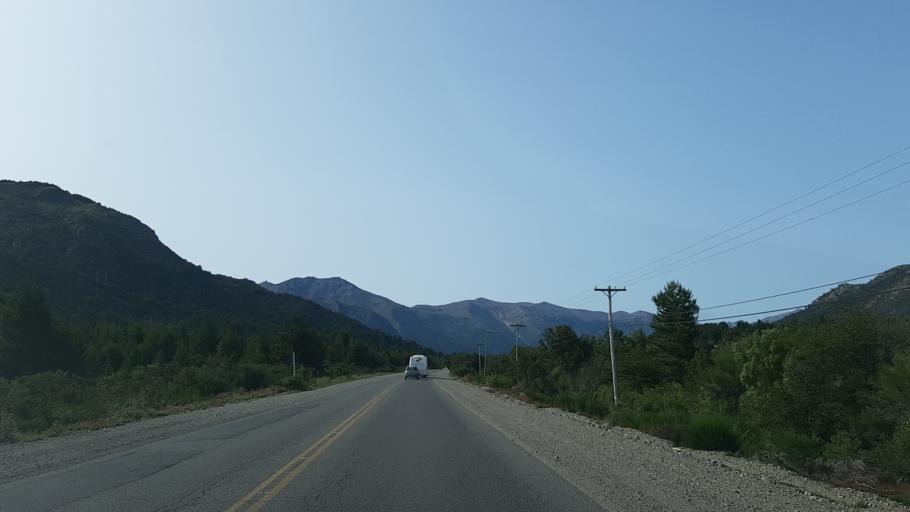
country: AR
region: Rio Negro
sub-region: Departamento de Bariloche
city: San Carlos de Bariloche
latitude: -41.1389
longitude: -71.4118
